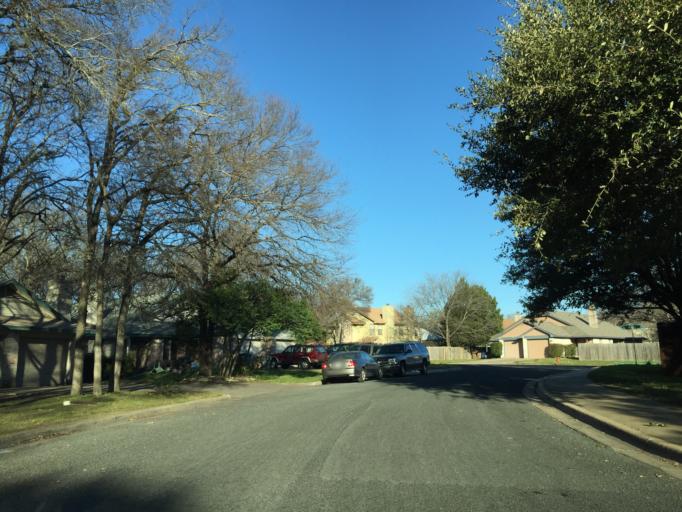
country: US
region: Texas
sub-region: Williamson County
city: Jollyville
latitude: 30.4388
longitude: -97.7674
